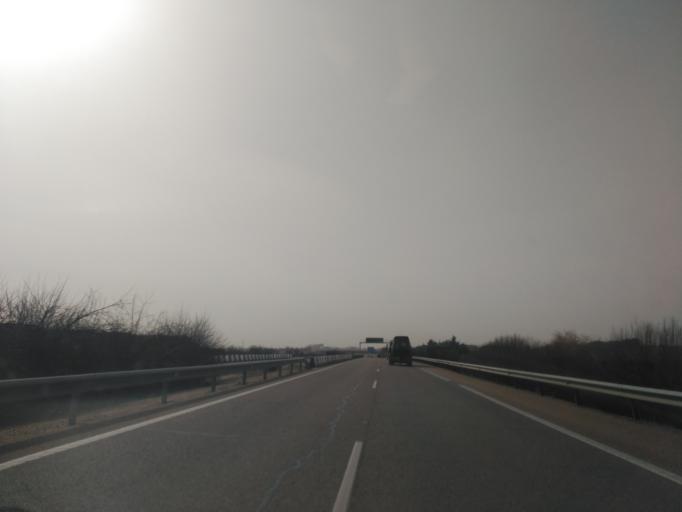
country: ES
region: Castille and Leon
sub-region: Provincia de Valladolid
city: Santovenia de Pisuerga
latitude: 41.6961
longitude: -4.7204
